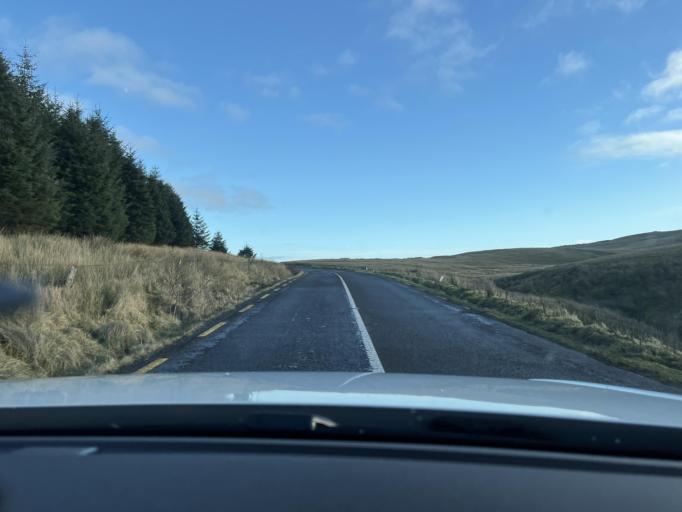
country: IE
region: Ulster
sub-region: An Cabhan
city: Ballyconnell
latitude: 54.1706
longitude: -7.8262
